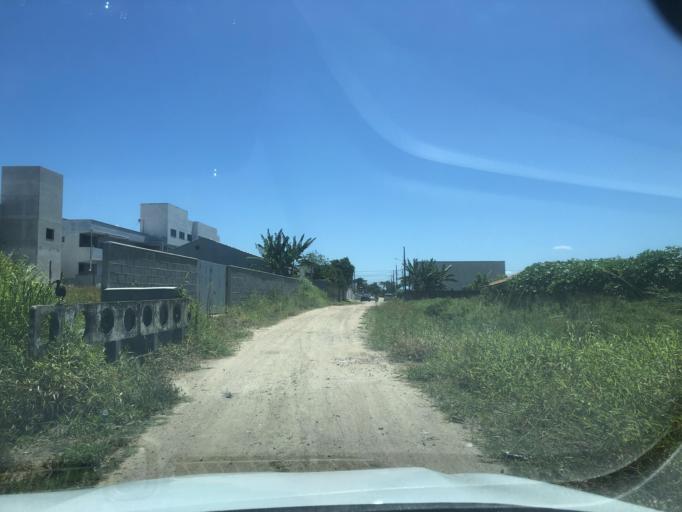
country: BR
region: Santa Catarina
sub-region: Sao Francisco Do Sul
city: Sao Francisco do Sul
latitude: -26.2228
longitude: -48.5245
